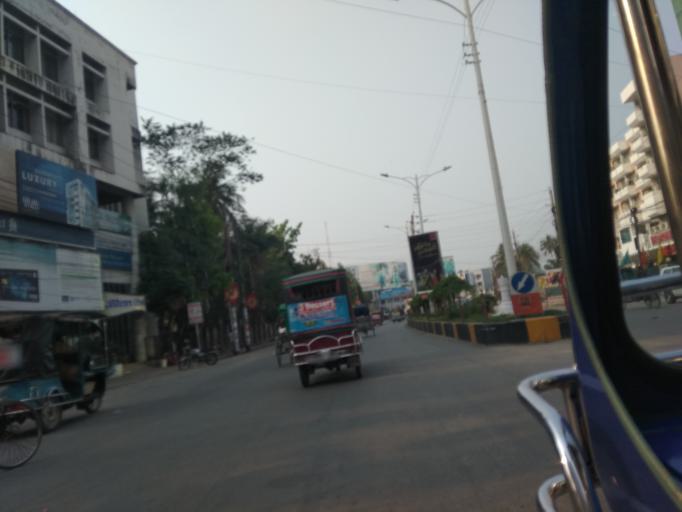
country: BD
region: Khulna
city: Khulna
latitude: 22.8207
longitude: 89.5529
